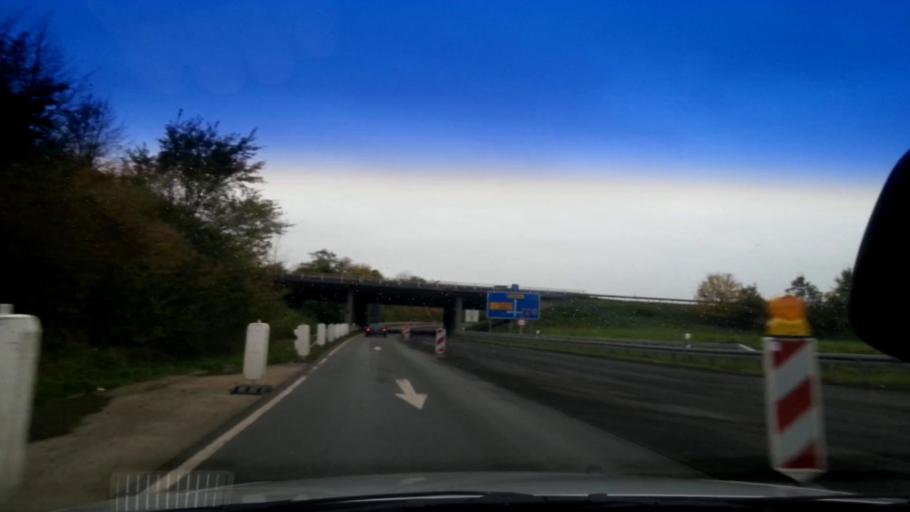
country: DE
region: Bavaria
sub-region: Upper Franconia
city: Schesslitz
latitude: 49.9834
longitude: 11.0456
